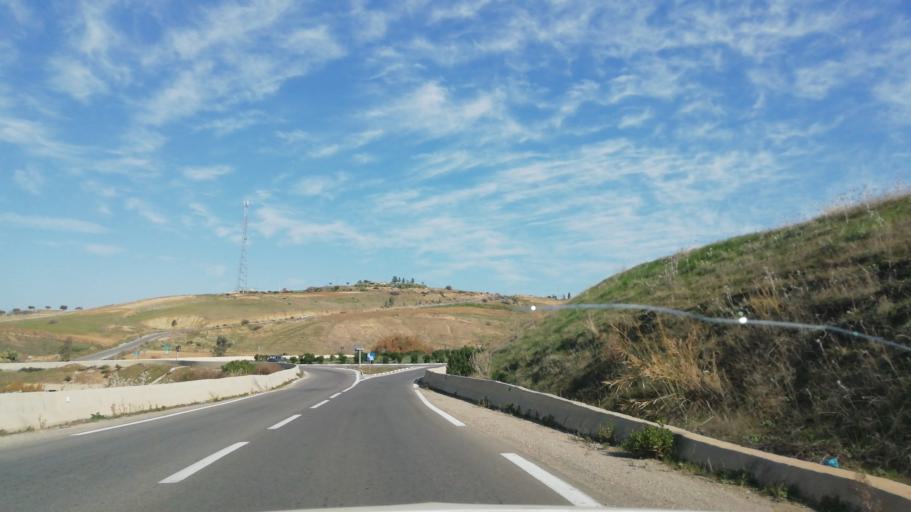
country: DZ
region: Tlemcen
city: Chetouane
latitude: 34.9801
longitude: -1.2382
